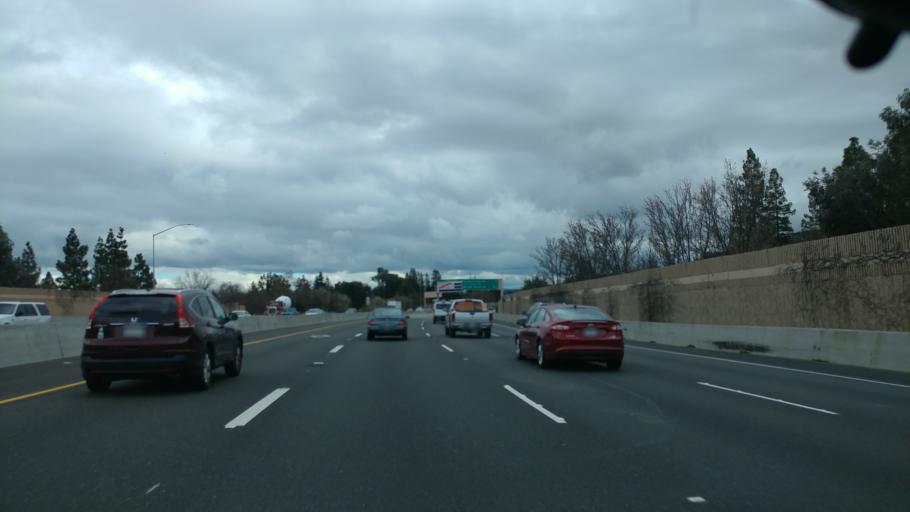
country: US
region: California
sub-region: Contra Costa County
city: Danville
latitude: 37.8245
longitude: -121.9945
